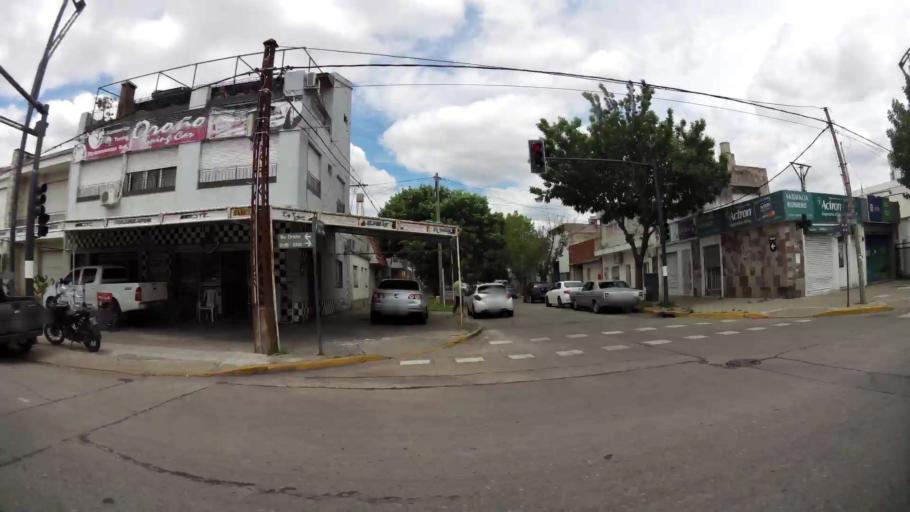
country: AR
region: Santa Fe
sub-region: Departamento de Rosario
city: Rosario
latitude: -32.9717
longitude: -60.6602
